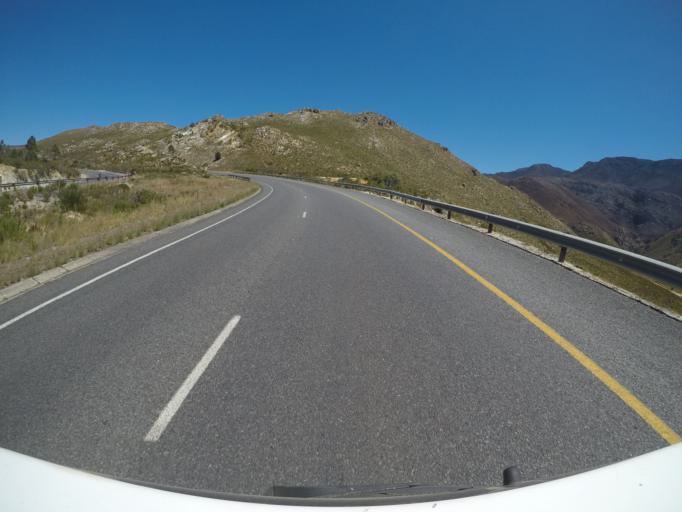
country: ZA
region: Western Cape
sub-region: Overberg District Municipality
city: Grabouw
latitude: -34.2181
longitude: 19.1887
